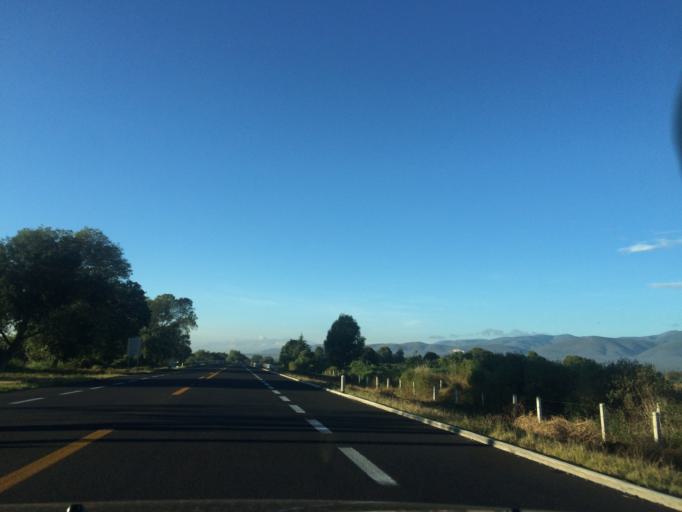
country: MX
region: Puebla
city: Santiago Miahuatlan
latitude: 18.5255
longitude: -97.4556
